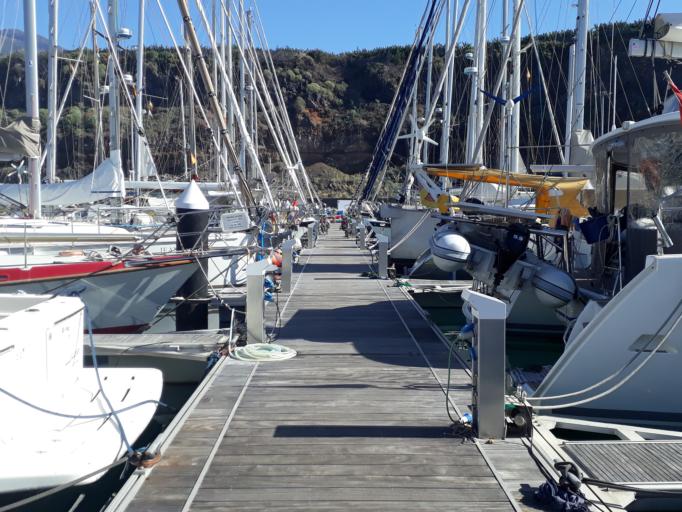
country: ES
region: Canary Islands
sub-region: Provincia de Santa Cruz de Tenerife
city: Tazacorte
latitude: 28.6440
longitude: -17.9437
